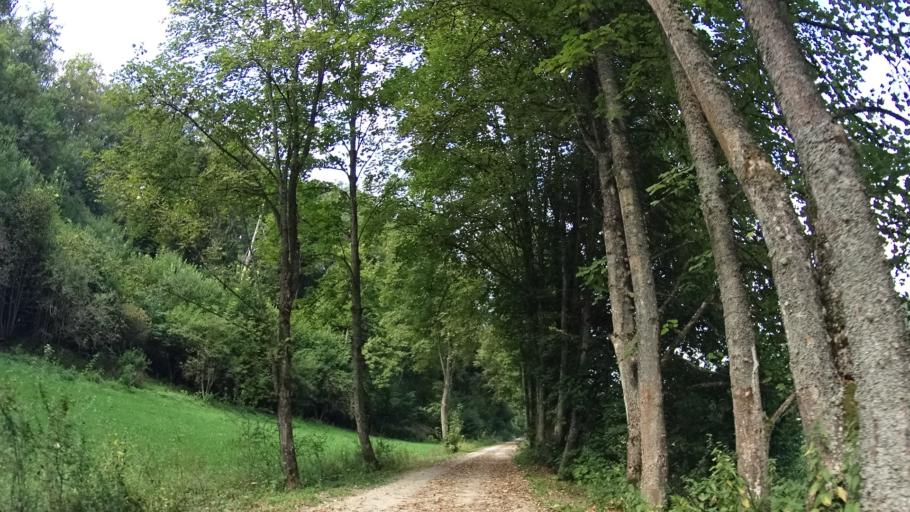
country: DE
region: Bavaria
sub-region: Lower Bavaria
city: Riedenburg
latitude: 48.9350
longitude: 11.6861
